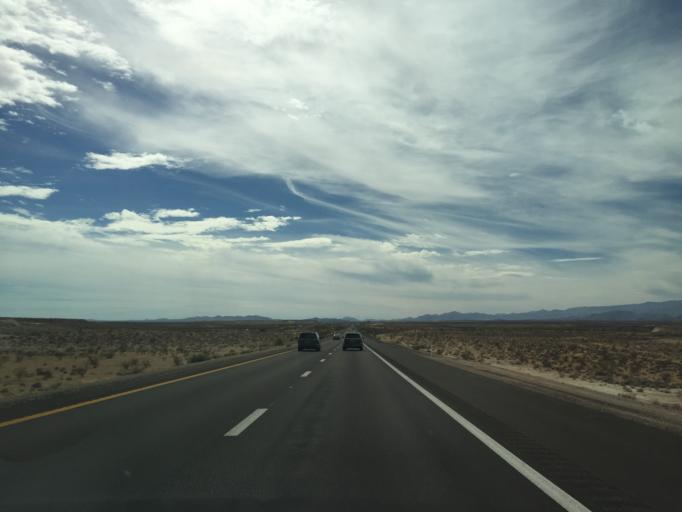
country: US
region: Nevada
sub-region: Clark County
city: Moapa Town
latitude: 36.5675
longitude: -114.6758
